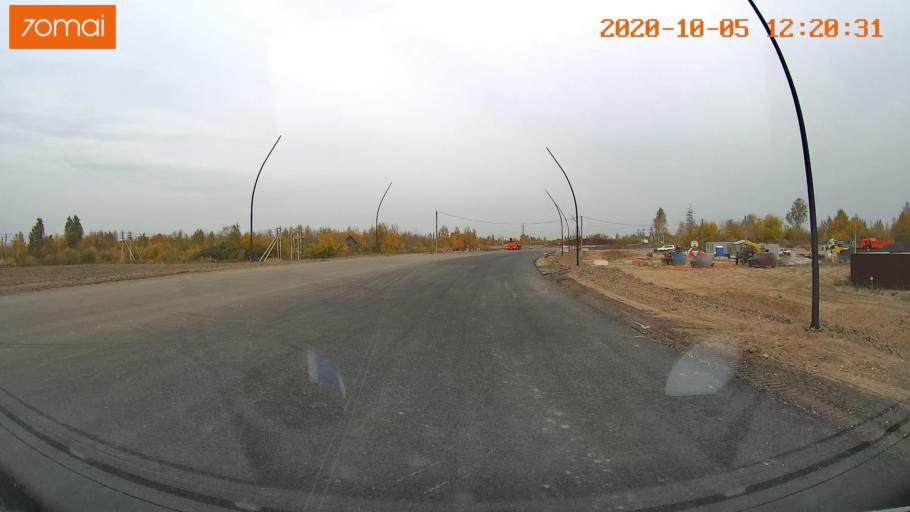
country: RU
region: Ivanovo
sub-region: Gorod Ivanovo
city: Ivanovo
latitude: 56.9642
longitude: 40.9307
